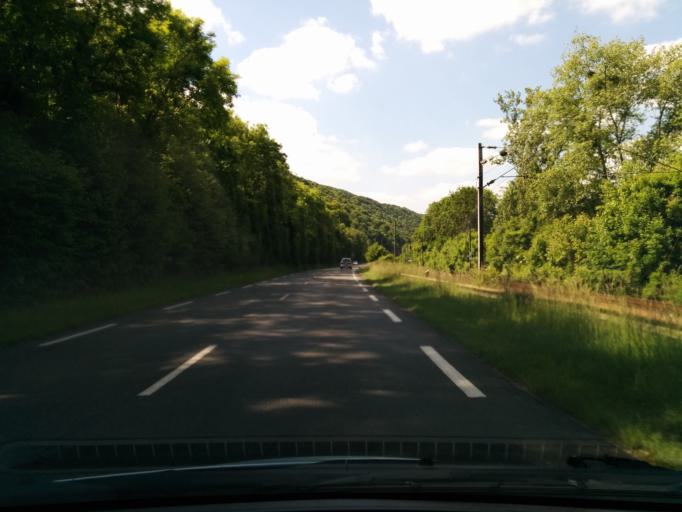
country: FR
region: Ile-de-France
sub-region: Departement des Yvelines
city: Bennecourt
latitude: 49.0402
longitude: 1.5365
